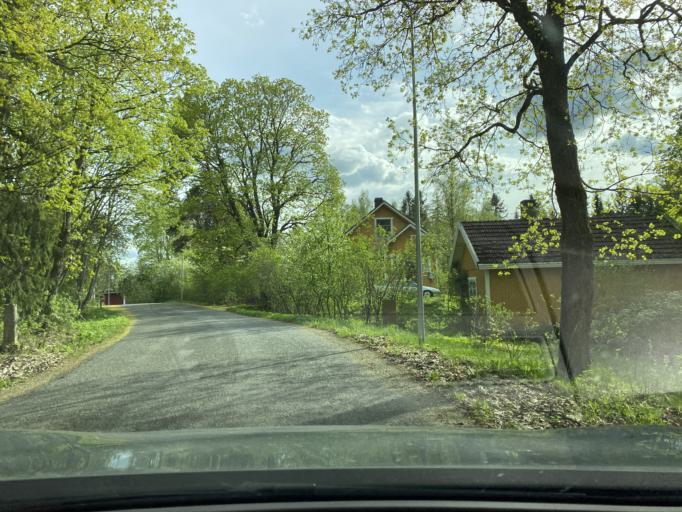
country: FI
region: Varsinais-Suomi
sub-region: Salo
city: Kiikala
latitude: 60.4579
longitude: 23.5484
